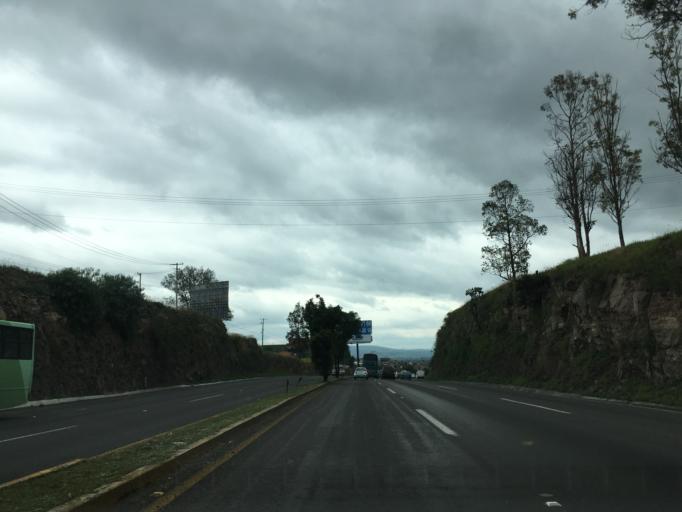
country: MX
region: Michoacan
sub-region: Tarimbaro
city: San Bernabe de las Canteras
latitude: 19.7591
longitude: -101.1674
